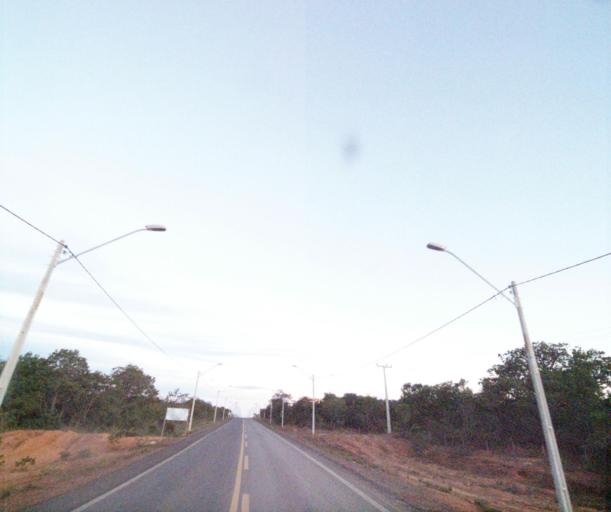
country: BR
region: Bahia
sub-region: Correntina
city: Correntina
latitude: -13.8186
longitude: -44.4800
